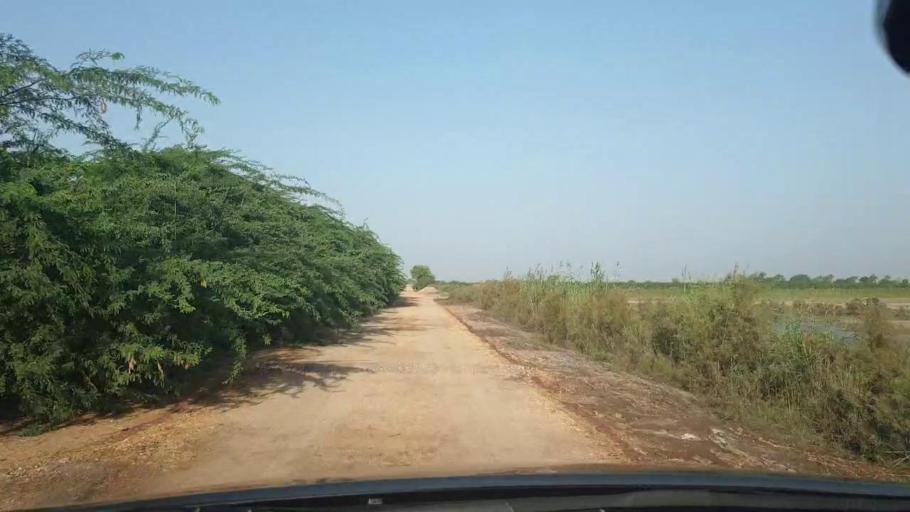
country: PK
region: Sindh
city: Tando Bago
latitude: 24.6452
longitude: 69.1344
